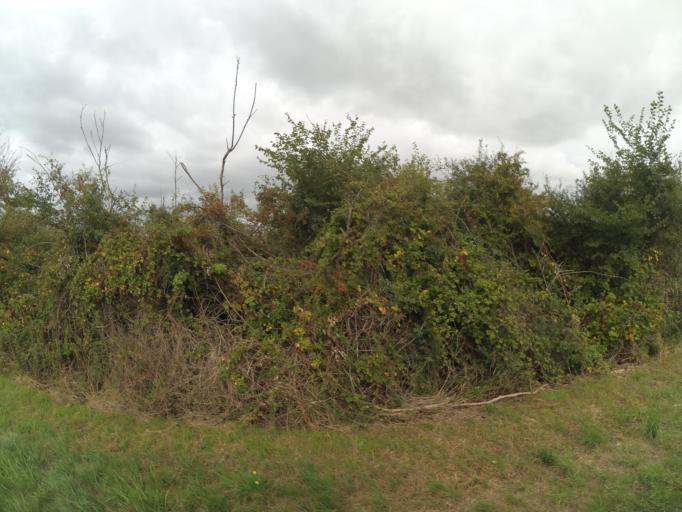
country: FR
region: Pays de la Loire
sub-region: Departement de la Vendee
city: Les Magnils-Reigniers
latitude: 46.4383
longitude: -1.2669
